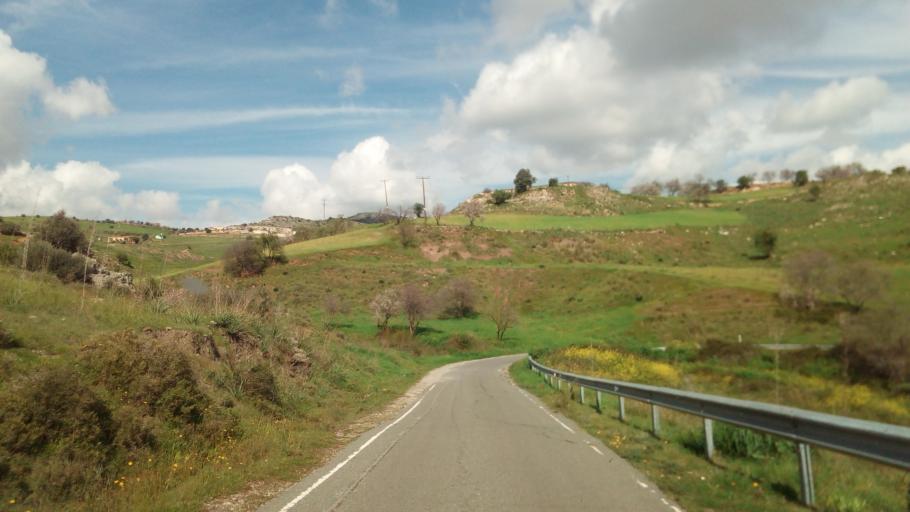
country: CY
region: Pafos
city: Mesogi
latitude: 34.7727
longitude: 32.5663
